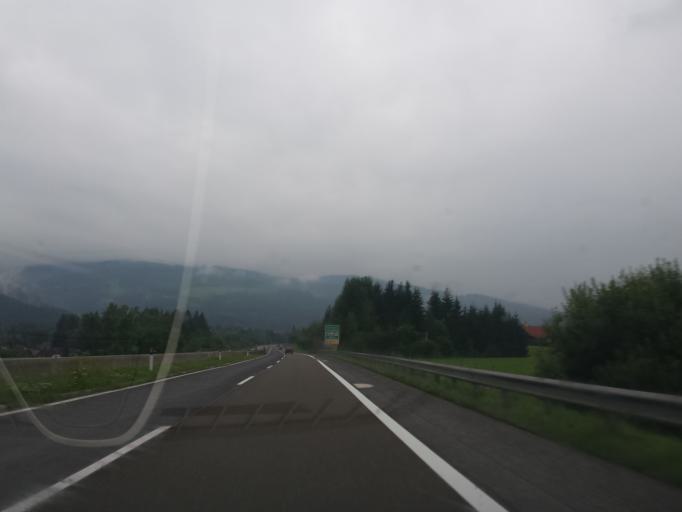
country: AT
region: Styria
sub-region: Politischer Bezirk Bruck-Muerzzuschlag
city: Krieglach
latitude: 47.5493
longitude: 15.5760
